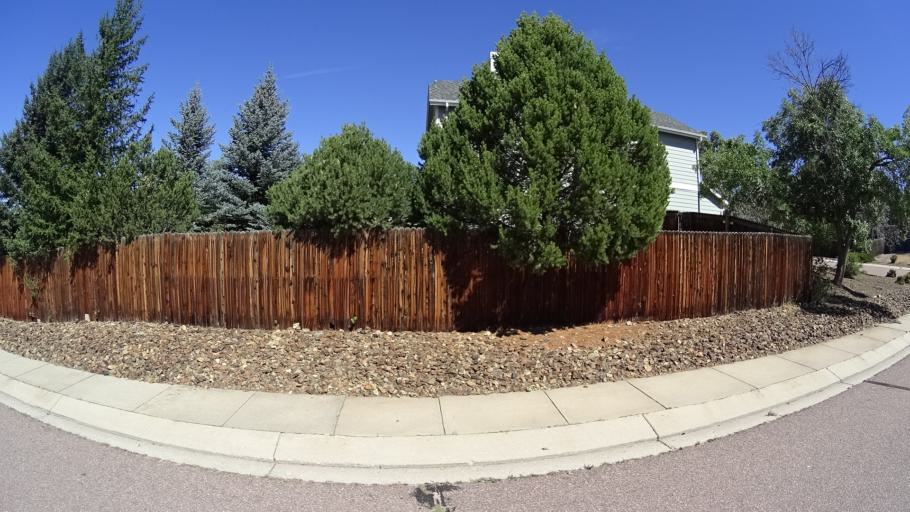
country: US
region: Colorado
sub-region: El Paso County
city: Black Forest
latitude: 38.9474
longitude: -104.7507
